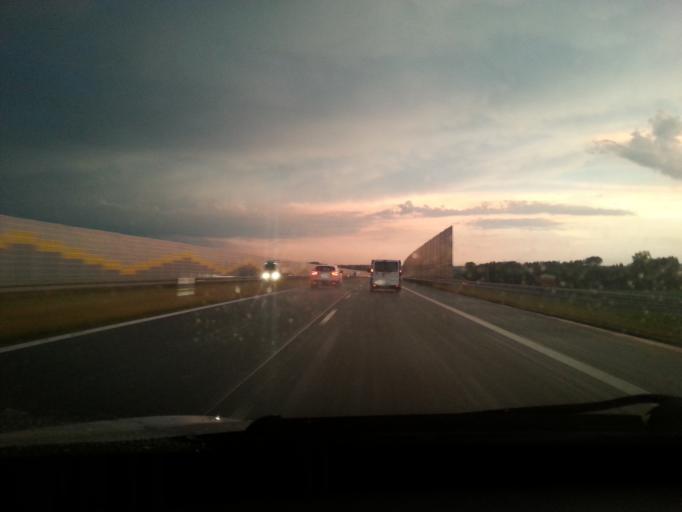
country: PL
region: Lodz Voivodeship
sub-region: Powiat laski
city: Lask
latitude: 51.5668
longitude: 19.1590
